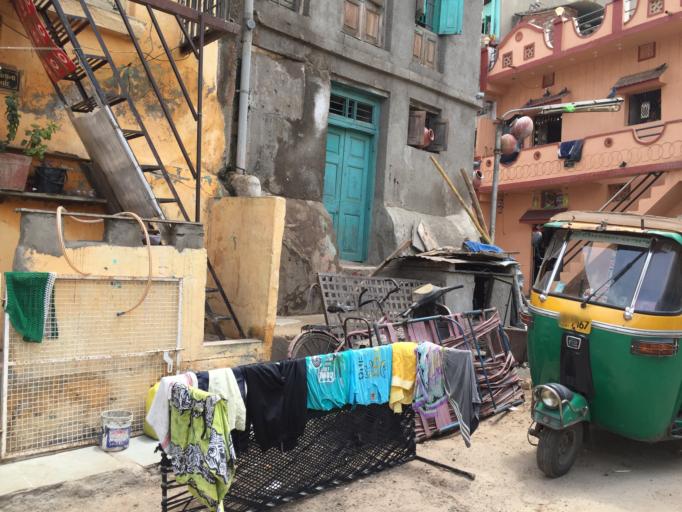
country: IN
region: Gujarat
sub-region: Ahmadabad
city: Ahmedabad
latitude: 23.0374
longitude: 72.5831
